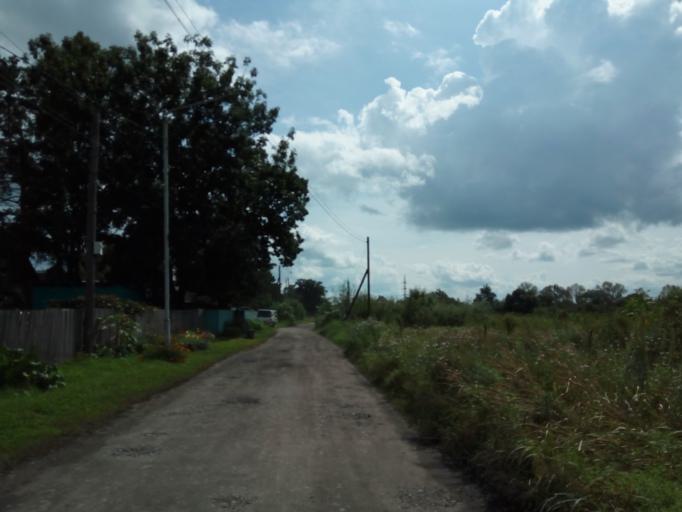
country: RU
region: Primorskiy
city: Dal'nerechensk
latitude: 45.9516
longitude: 133.8165
